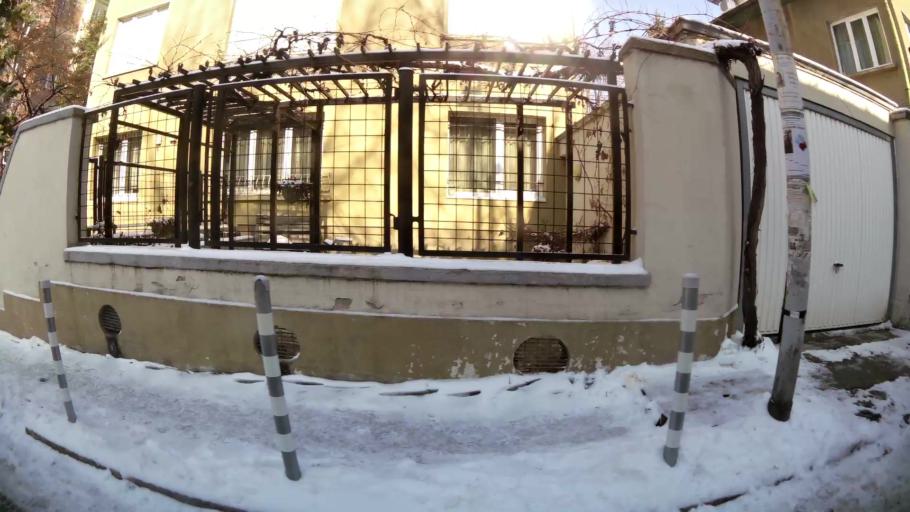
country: BG
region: Sofia-Capital
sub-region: Stolichna Obshtina
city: Sofia
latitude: 42.6775
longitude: 23.3254
